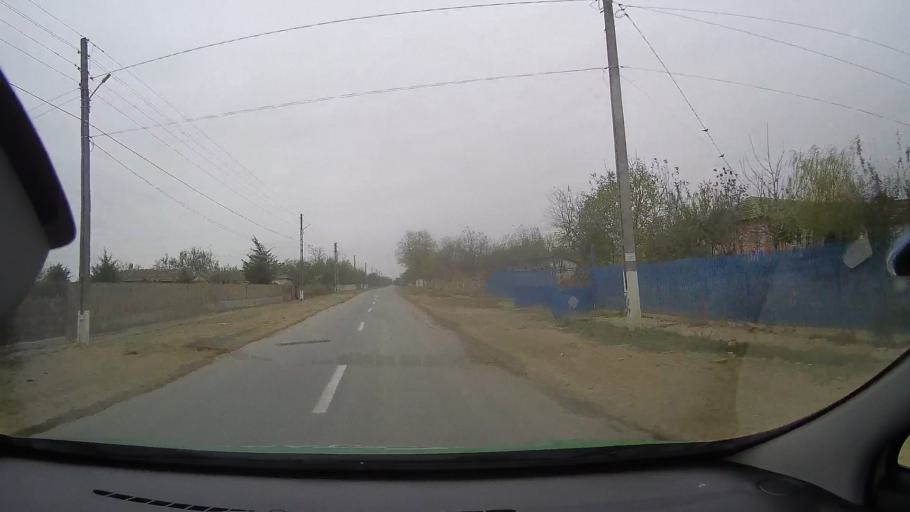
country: RO
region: Constanta
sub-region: Comuna Vulturu
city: Vulturu
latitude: 44.6419
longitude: 28.2734
